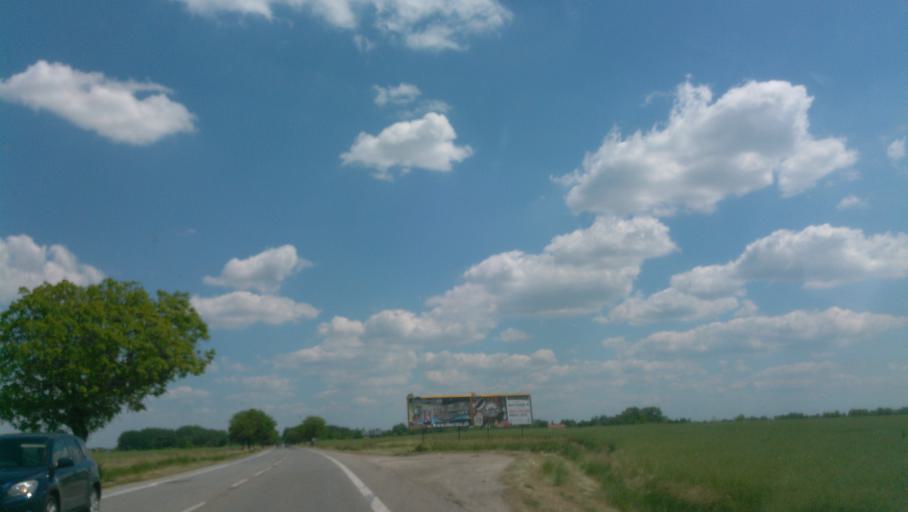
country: SK
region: Trnavsky
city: Samorin
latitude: 48.0101
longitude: 17.3547
